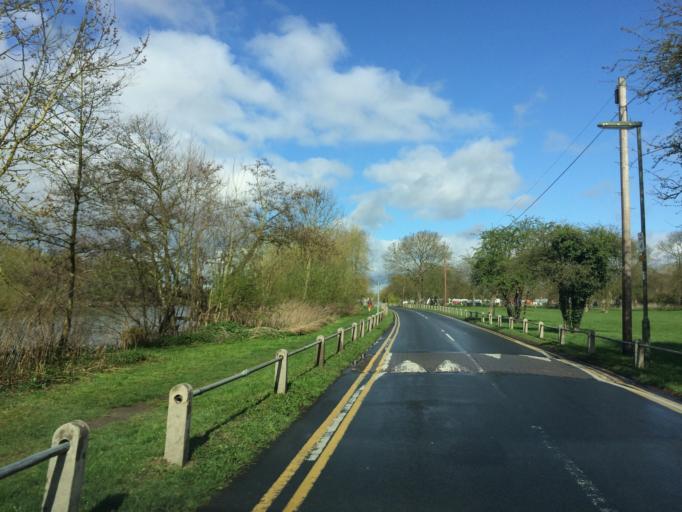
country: GB
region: England
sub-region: Surrey
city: Chertsey
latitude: 51.3972
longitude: -0.4875
